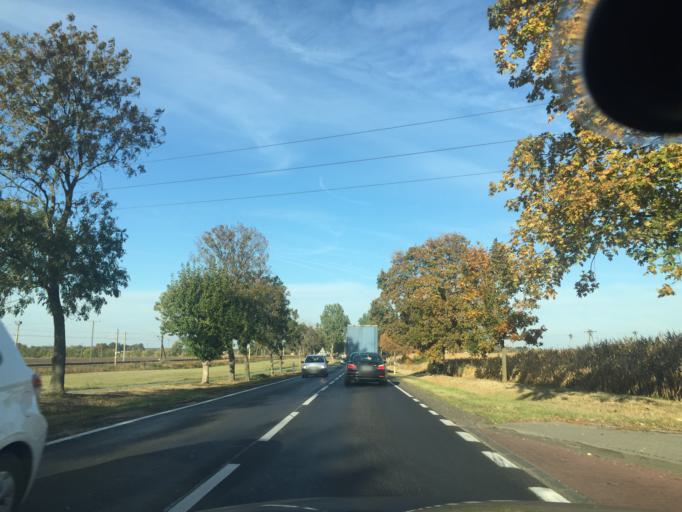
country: PL
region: Kujawsko-Pomorskie
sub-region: Powiat inowroclawski
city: Gniewkowo
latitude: 52.8808
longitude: 18.3847
